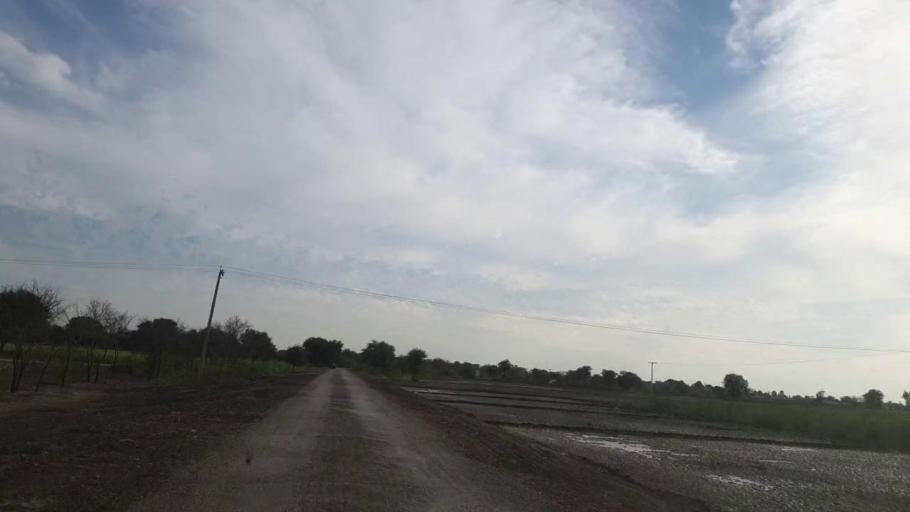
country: PK
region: Sindh
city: Pithoro
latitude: 25.6428
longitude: 69.3614
